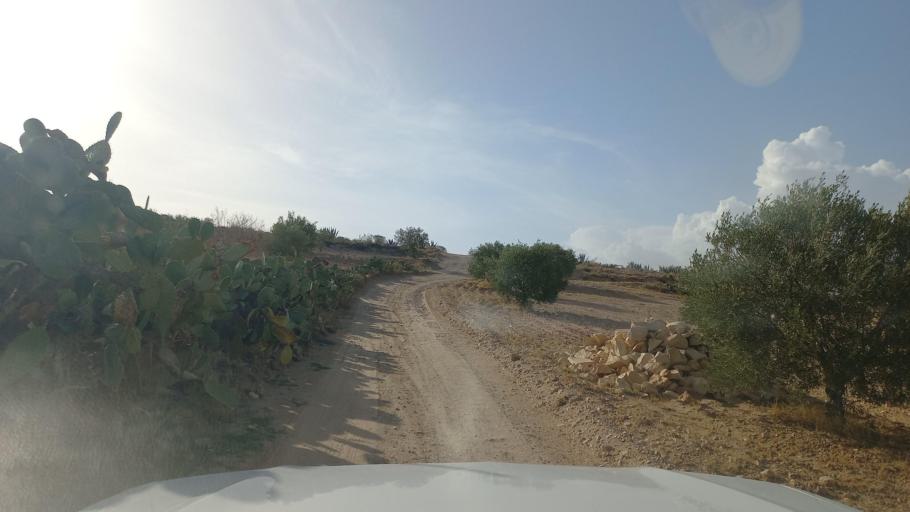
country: TN
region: Al Qasrayn
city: Kasserine
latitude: 35.2343
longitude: 8.9186
